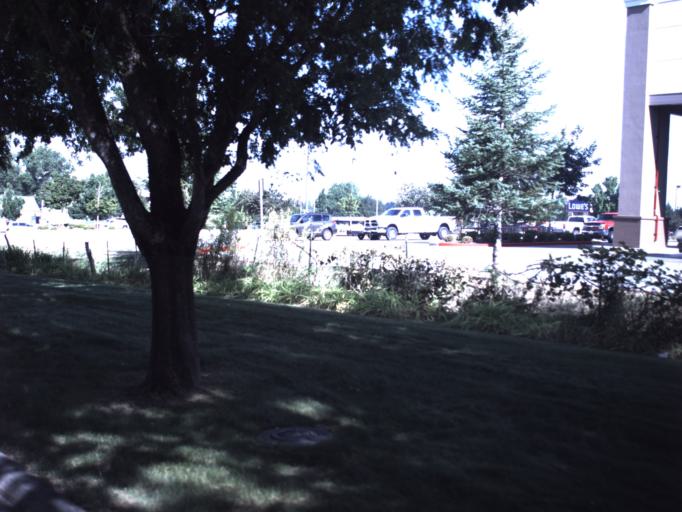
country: US
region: Utah
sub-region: Weber County
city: Harrisville
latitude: 41.2645
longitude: -111.9680
